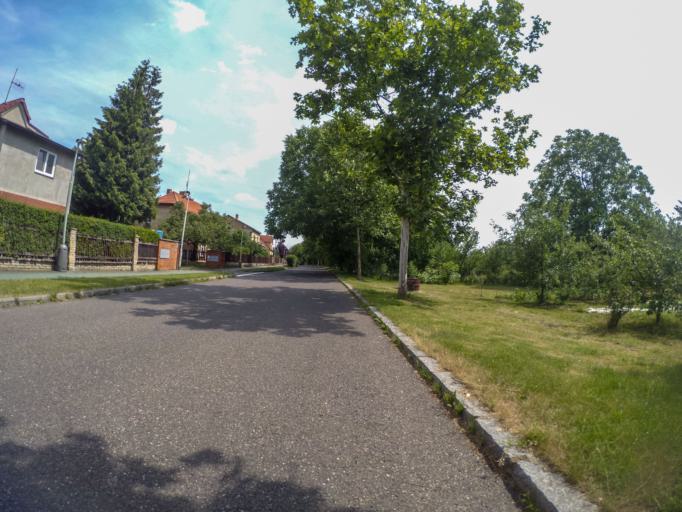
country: CZ
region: Praha
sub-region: Praha 19
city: Kbely
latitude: 50.1283
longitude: 14.5563
